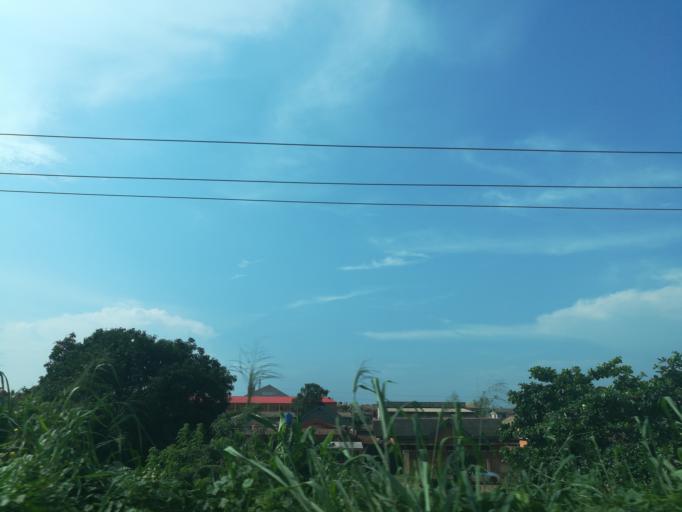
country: NG
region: Lagos
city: Ikorodu
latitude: 6.6302
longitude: 3.5160
